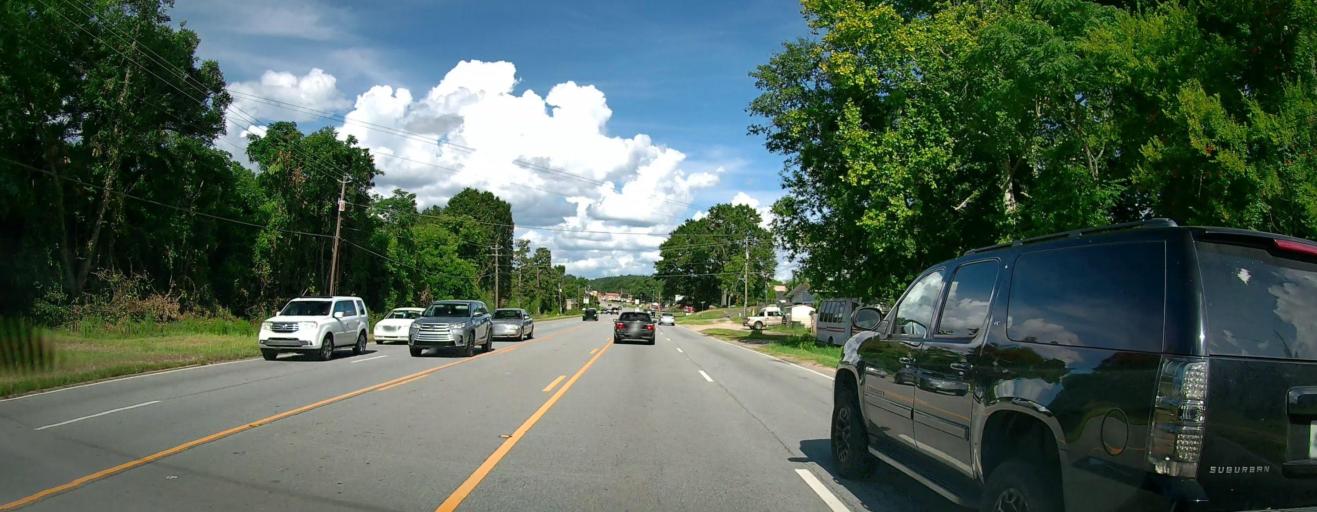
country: US
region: Alabama
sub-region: Russell County
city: Ladonia
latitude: 32.4679
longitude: -85.0755
